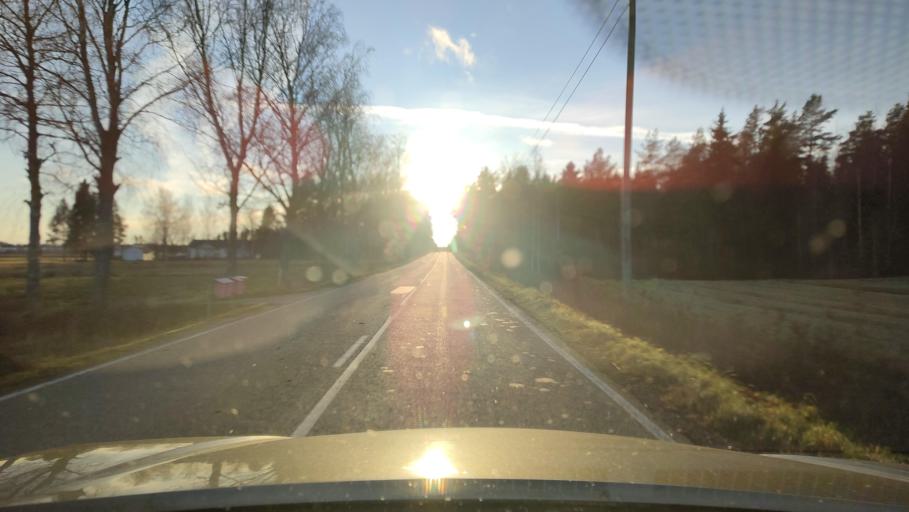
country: FI
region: Ostrobothnia
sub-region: Vaasa
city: Malax
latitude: 62.6996
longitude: 21.5798
